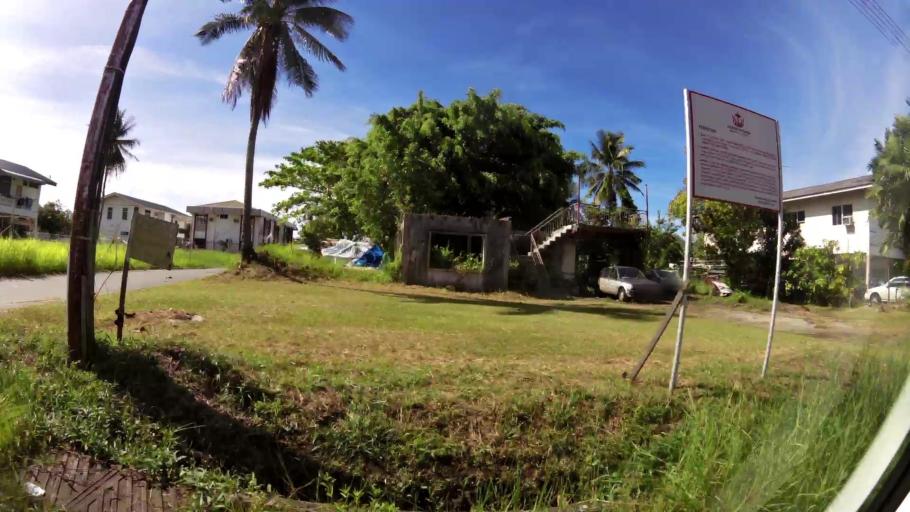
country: BN
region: Belait
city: Kuala Belait
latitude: 4.5864
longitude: 114.2093
